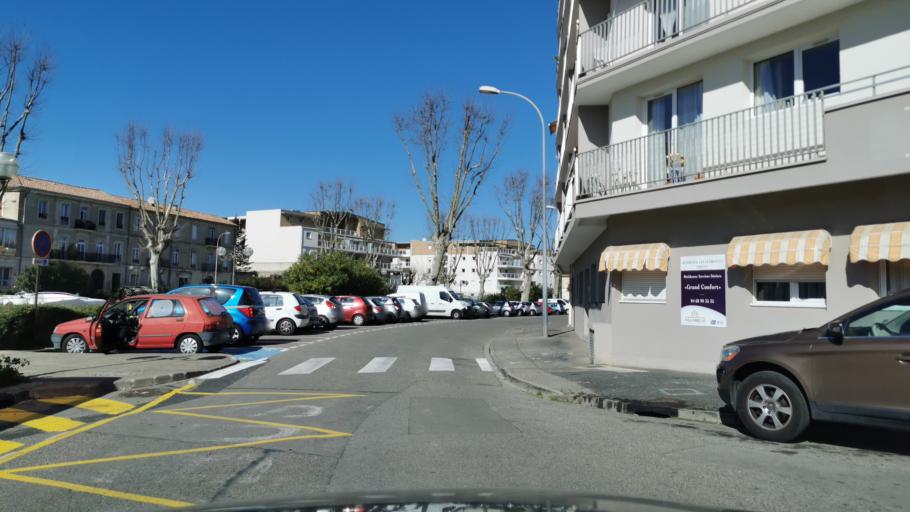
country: FR
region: Languedoc-Roussillon
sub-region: Departement de l'Aude
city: Narbonne
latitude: 43.1880
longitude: 2.9970
